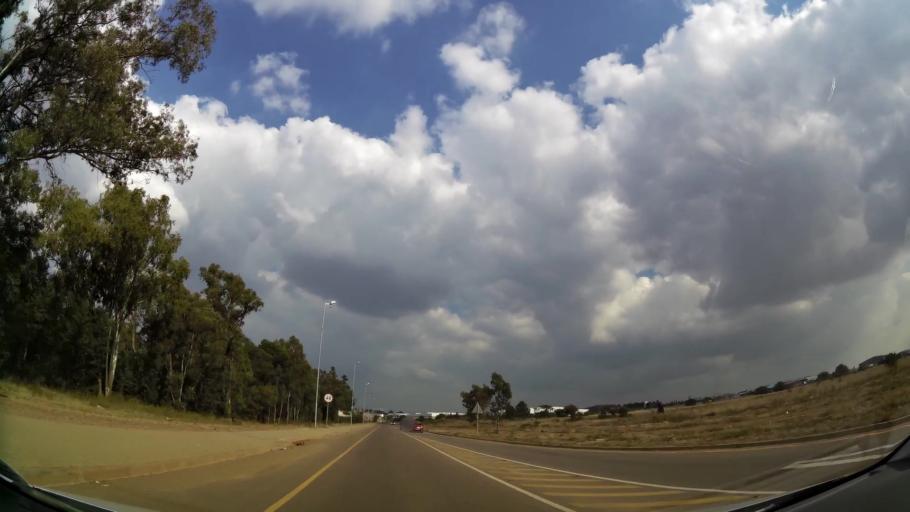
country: ZA
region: Gauteng
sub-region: City of Tshwane Metropolitan Municipality
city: Centurion
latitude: -25.8975
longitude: 28.1689
